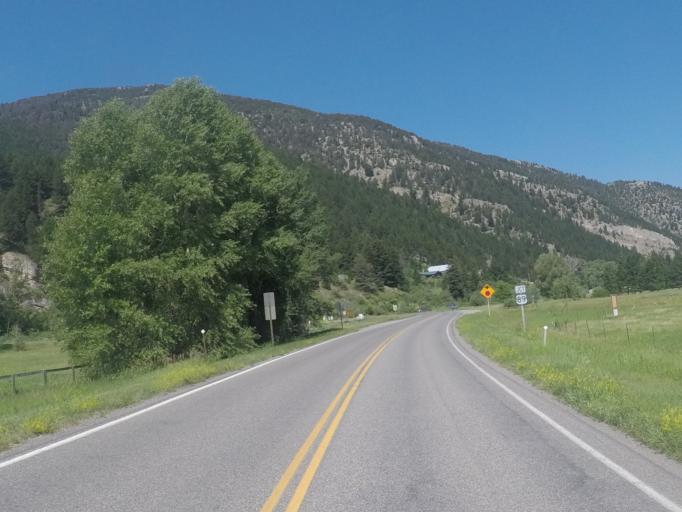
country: US
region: Montana
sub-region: Park County
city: Livingston
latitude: 45.5976
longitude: -110.5703
